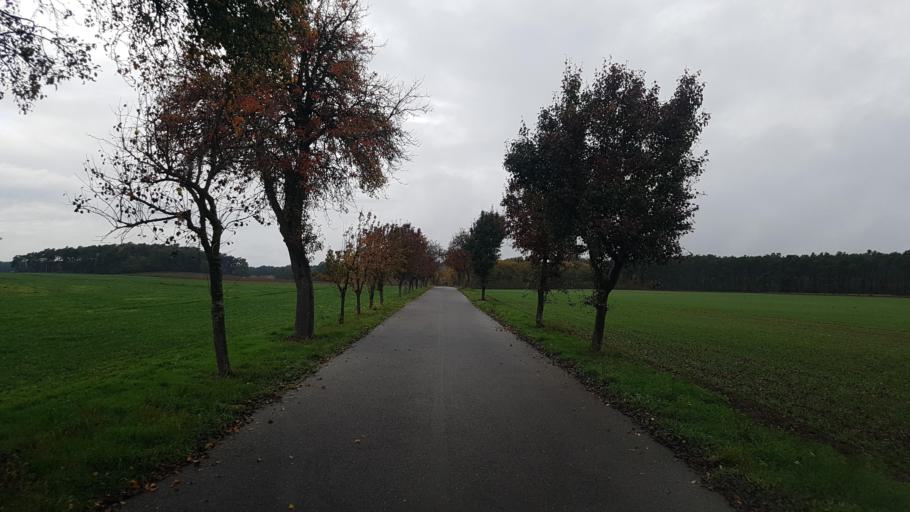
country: DE
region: Brandenburg
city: Schlieben
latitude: 51.7313
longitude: 13.3629
